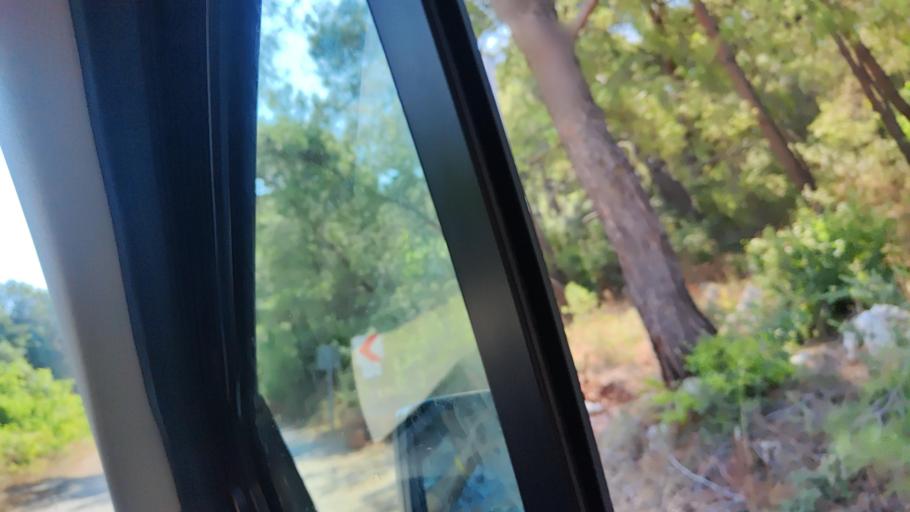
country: TR
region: Mugla
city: Sarigerme
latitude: 36.7076
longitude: 28.6951
